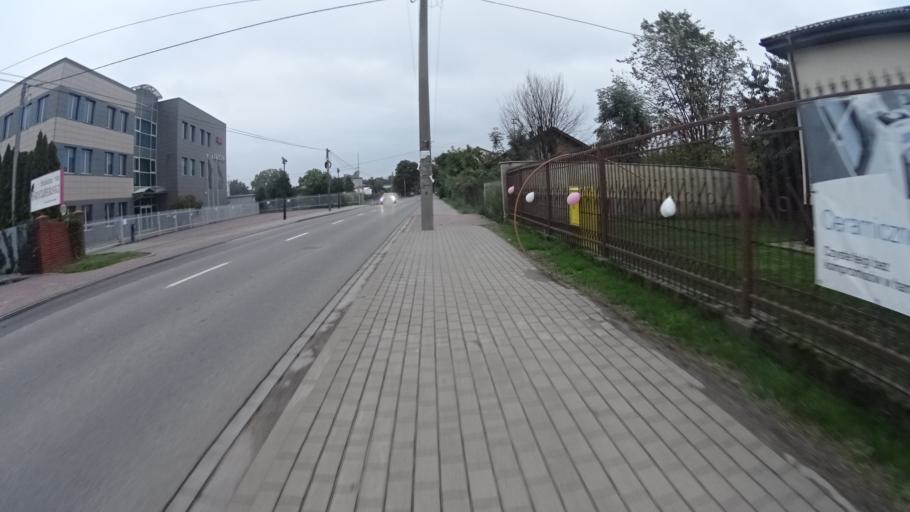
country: PL
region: Masovian Voivodeship
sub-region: Powiat warszawski zachodni
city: Babice
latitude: 52.2286
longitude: 20.8429
